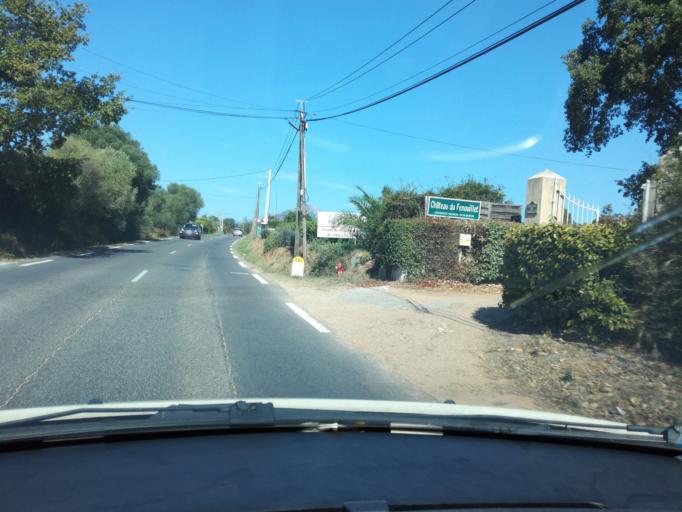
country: FR
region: Provence-Alpes-Cote d'Azur
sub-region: Departement du Var
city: La Crau
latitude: 43.1280
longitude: 6.0949
